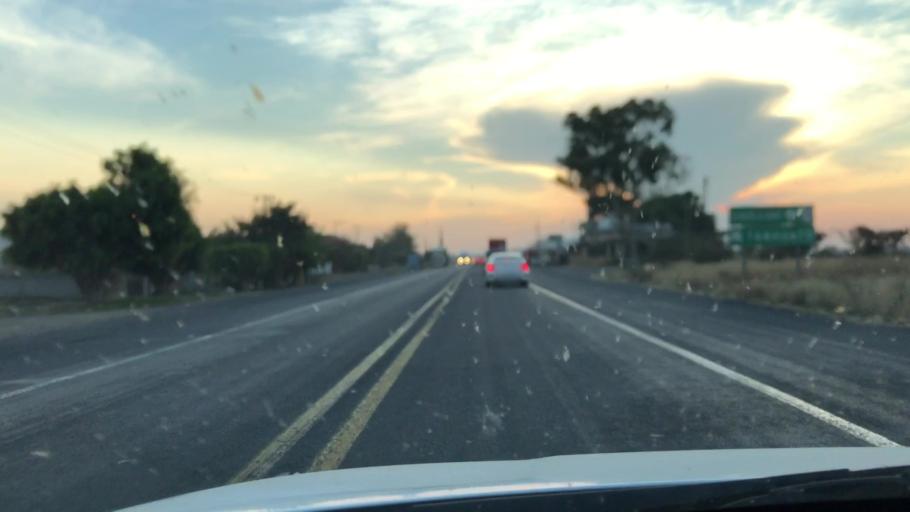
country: MX
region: Michoacan
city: Tanhuato de Guerrero
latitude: 20.3011
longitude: -102.3230
